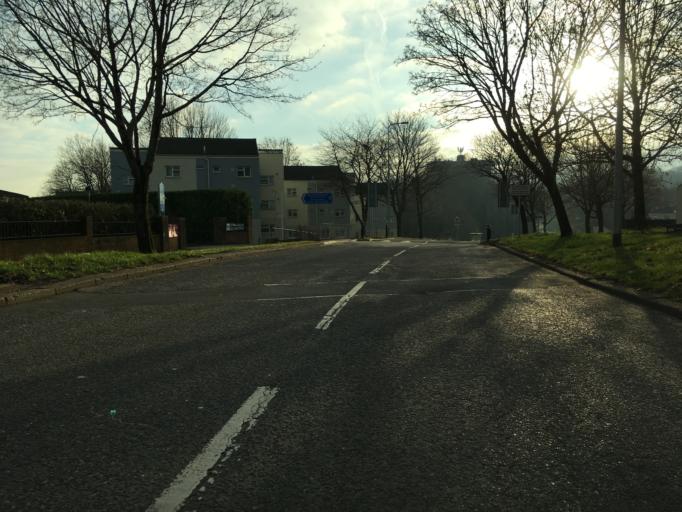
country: GB
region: Wales
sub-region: Cardiff
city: Cardiff
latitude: 51.5164
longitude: -3.1515
